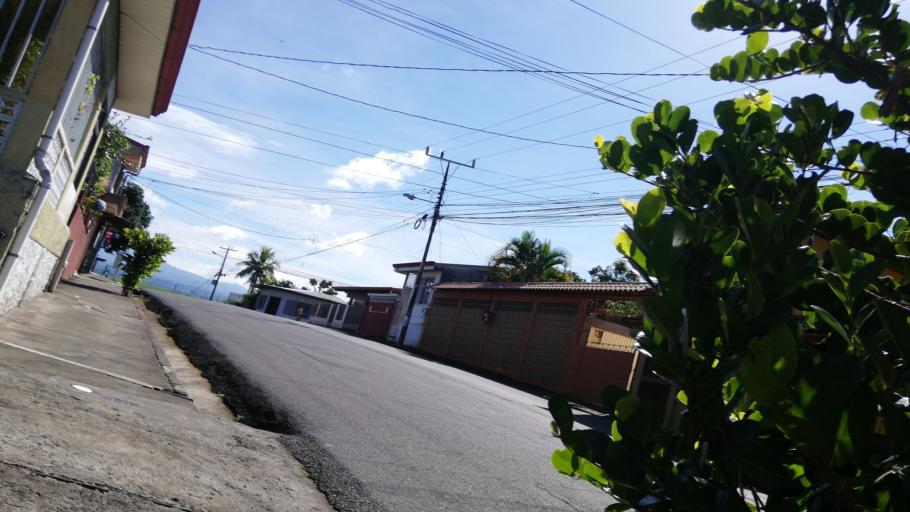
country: CR
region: Alajuela
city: San Juan
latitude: 10.0699
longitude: -84.3103
